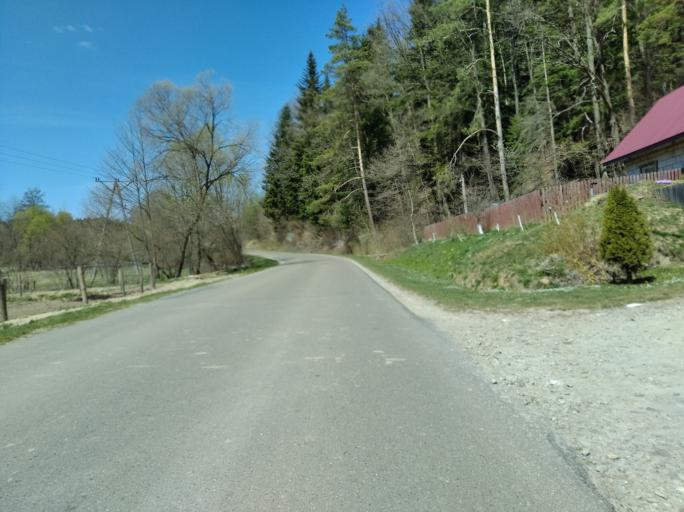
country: PL
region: Subcarpathian Voivodeship
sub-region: Powiat brzozowski
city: Jablonka
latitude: 49.7418
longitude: 22.0789
